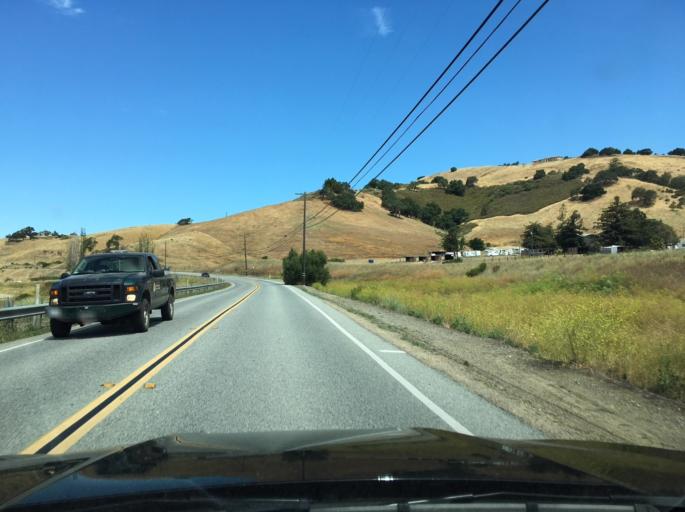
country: US
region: California
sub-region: Santa Clara County
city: Seven Trees
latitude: 37.1871
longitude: -121.7722
